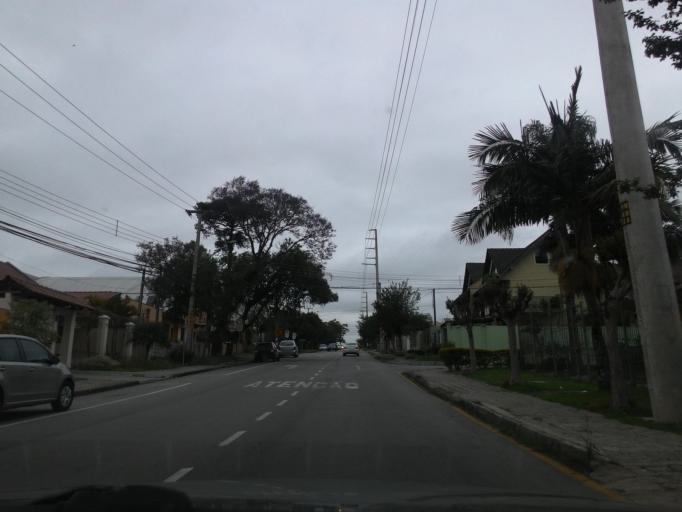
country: BR
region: Parana
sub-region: Curitiba
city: Curitiba
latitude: -25.4584
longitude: -49.2379
